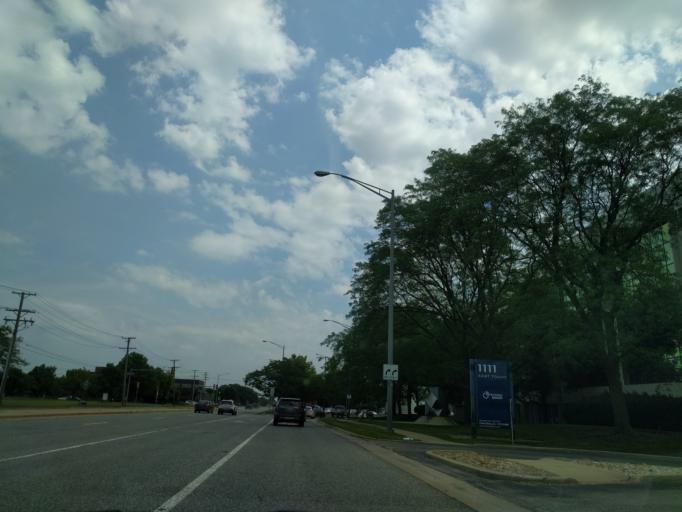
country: US
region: Illinois
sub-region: Cook County
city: Rosemont
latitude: 42.0091
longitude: -87.8967
